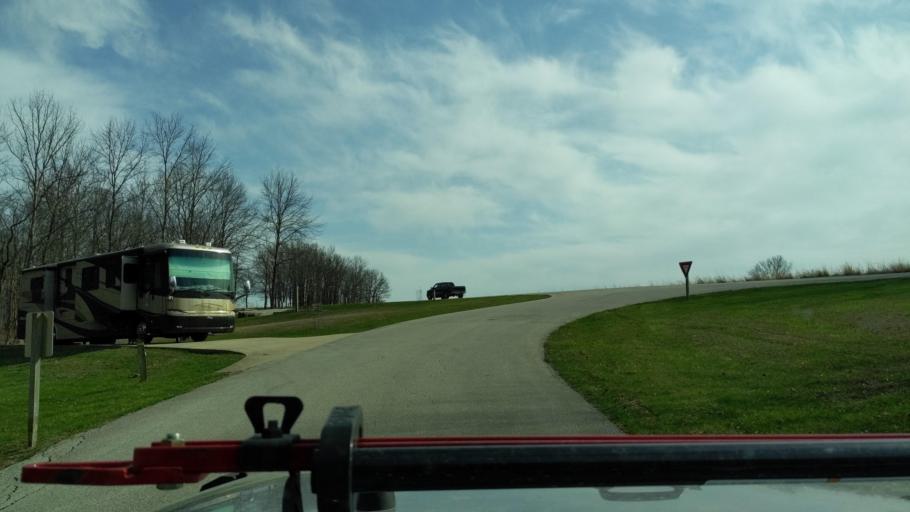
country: US
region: Missouri
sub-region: Macon County
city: Macon
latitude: 39.7709
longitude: -92.5215
